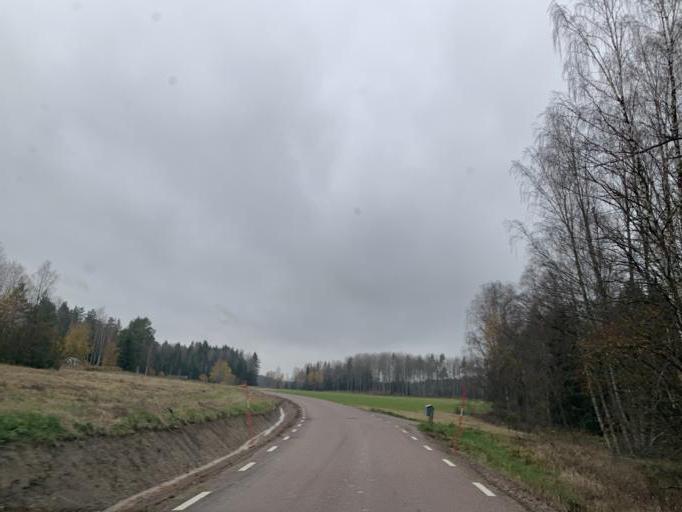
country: SE
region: Vaestmanland
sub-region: Kopings Kommun
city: Koping
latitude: 59.6448
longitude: 16.0651
